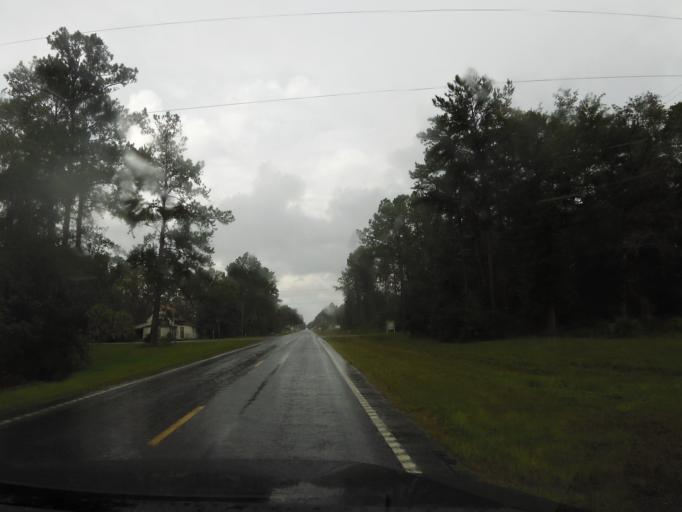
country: US
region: Florida
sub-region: Nassau County
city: Callahan
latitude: 30.5169
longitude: -82.0370
